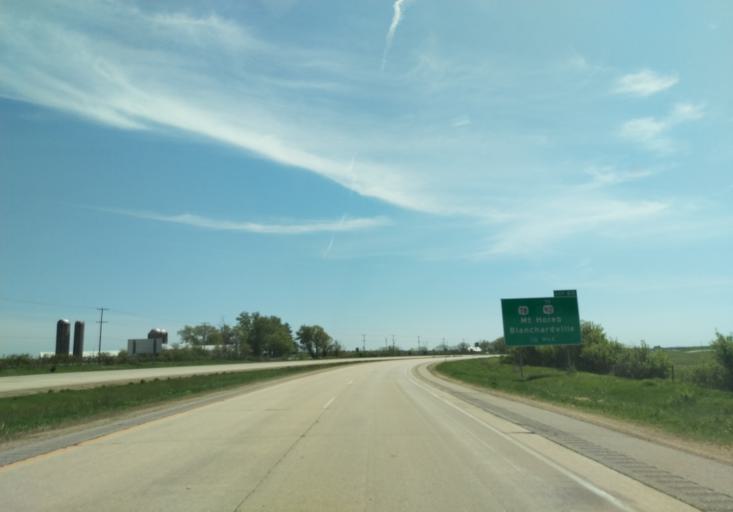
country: US
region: Wisconsin
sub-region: Dane County
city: Mount Horeb
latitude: 43.0066
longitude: -89.7751
